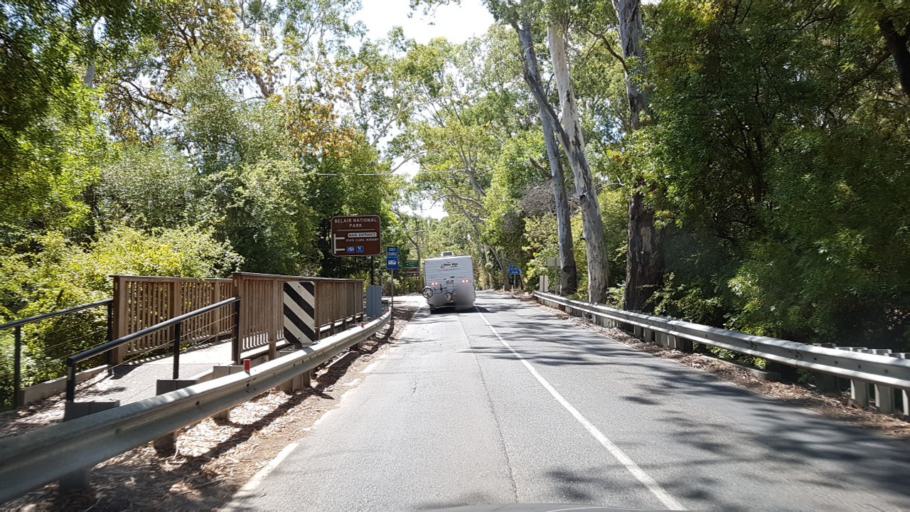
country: AU
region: South Australia
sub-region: Mitcham
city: Belair
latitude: -35.0099
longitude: 138.6332
